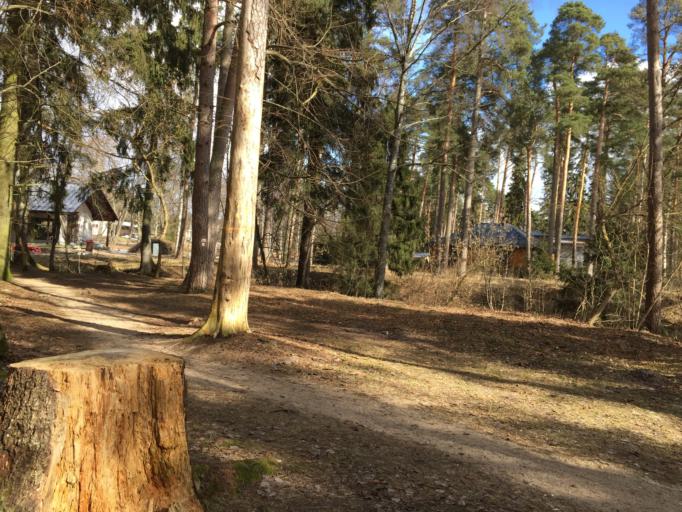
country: LV
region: Valmieras Rajons
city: Valmiera
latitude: 57.5427
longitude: 25.4497
